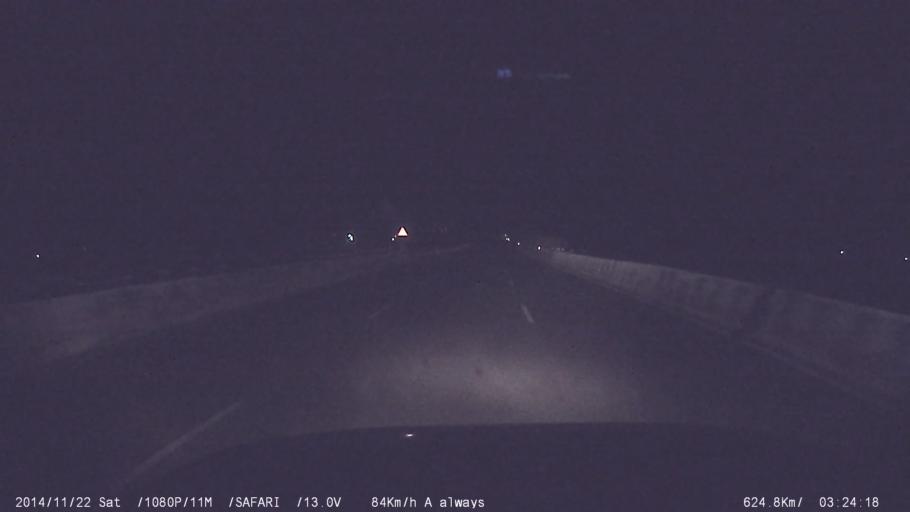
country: IN
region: Tamil Nadu
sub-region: Salem
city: Ilampillai
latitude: 11.5451
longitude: 77.9836
